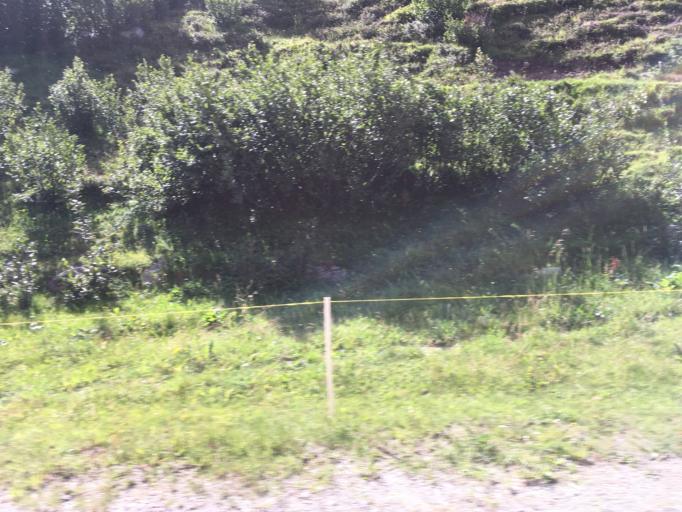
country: CH
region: Grisons
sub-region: Maloja District
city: Silvaplana
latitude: 46.4620
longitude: 9.6839
